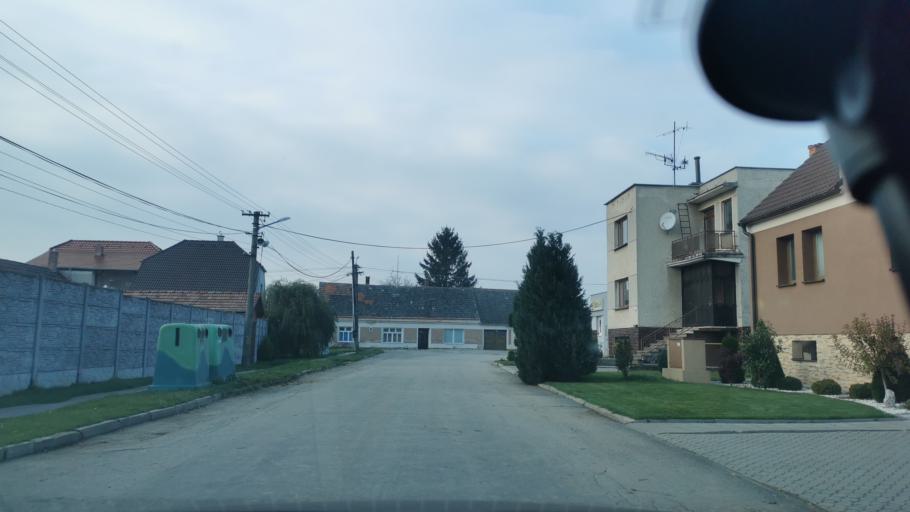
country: SK
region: Trnavsky
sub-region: Okres Skalica
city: Skalica
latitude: 48.7701
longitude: 17.2826
